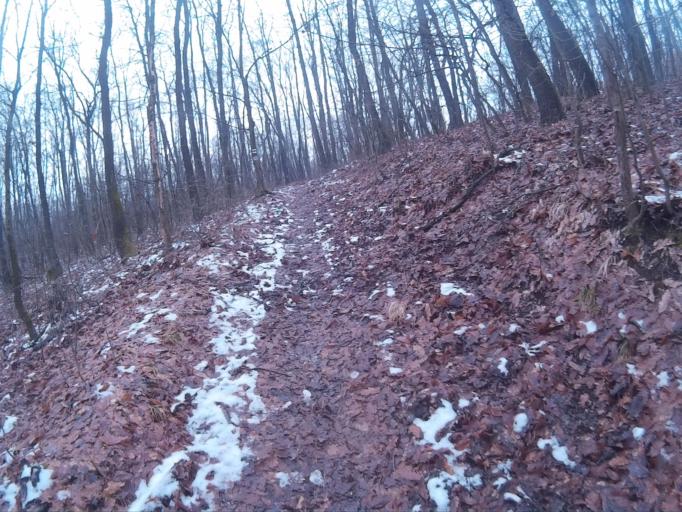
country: HU
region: Komarom-Esztergom
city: Nyergesujfalu
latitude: 47.7051
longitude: 18.5530
